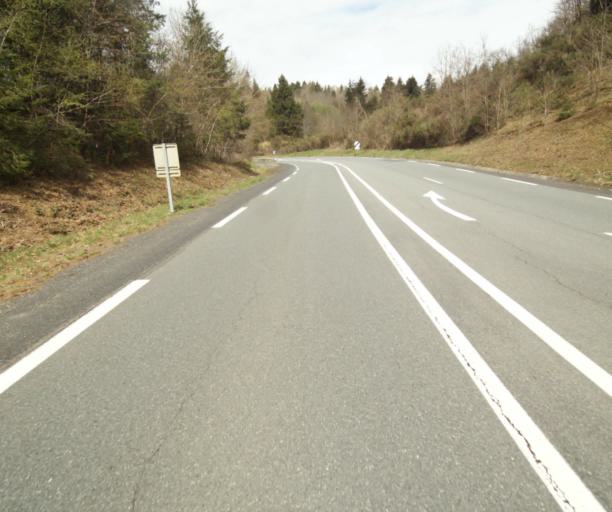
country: FR
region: Limousin
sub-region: Departement de la Correze
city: Sainte-Fortunade
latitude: 45.1934
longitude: 1.8397
